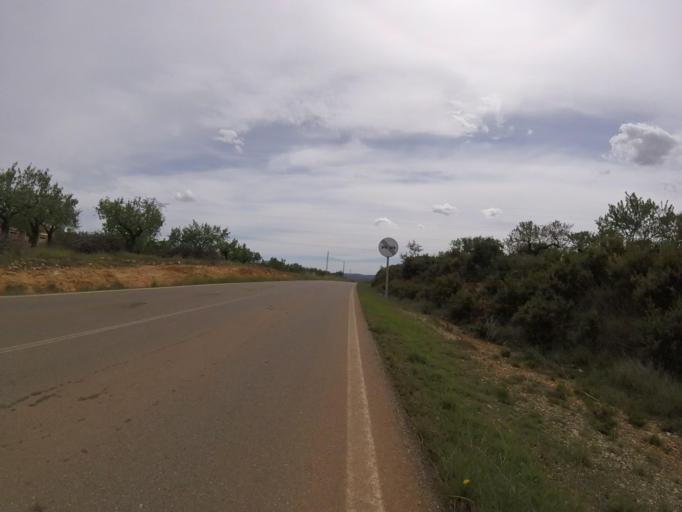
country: ES
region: Valencia
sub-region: Provincia de Castello
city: Cabanes
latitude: 40.1701
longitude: -0.0008
